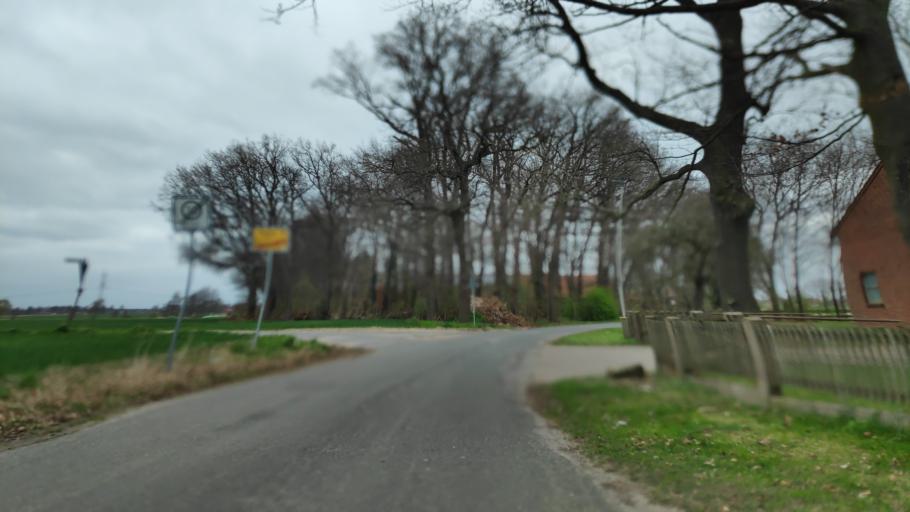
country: DE
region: North Rhine-Westphalia
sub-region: Regierungsbezirk Detmold
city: Minden
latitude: 52.3385
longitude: 8.8564
